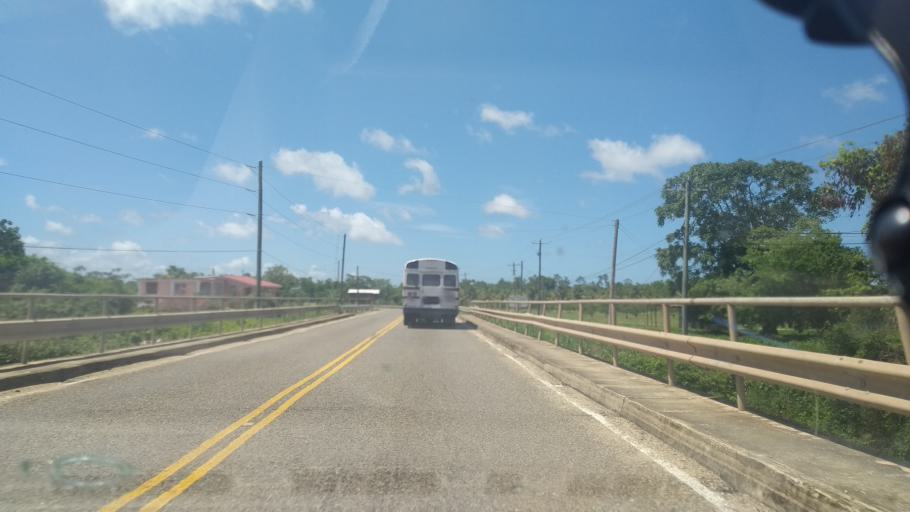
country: BZ
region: Stann Creek
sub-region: Dangriga
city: Dangriga
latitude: 16.9995
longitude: -88.3028
